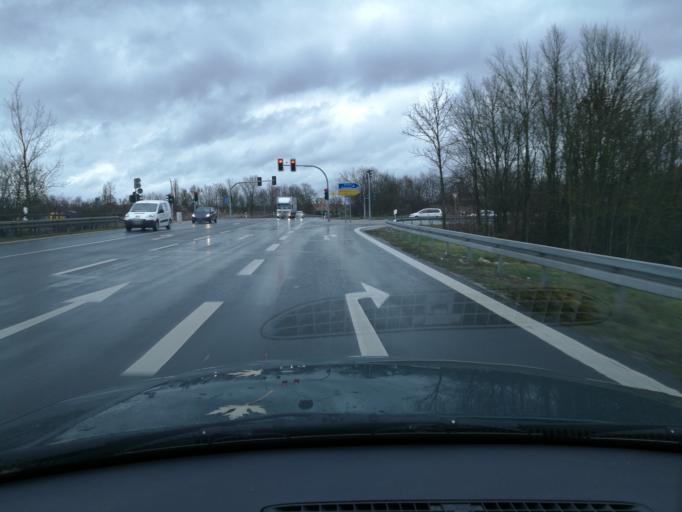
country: DE
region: Bavaria
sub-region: Regierungsbezirk Mittelfranken
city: Seukendorf
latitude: 49.4829
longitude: 10.8731
